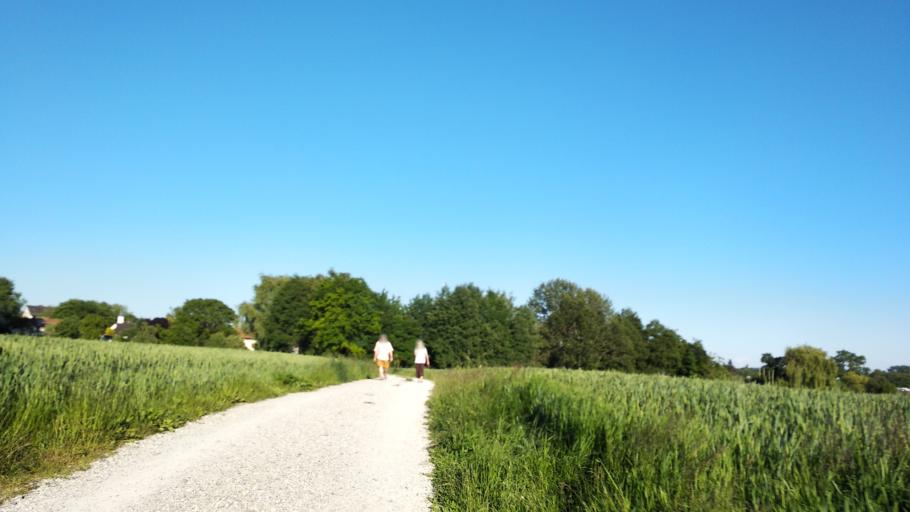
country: DE
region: Bavaria
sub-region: Upper Bavaria
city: Zorneding
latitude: 48.1044
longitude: 11.8212
